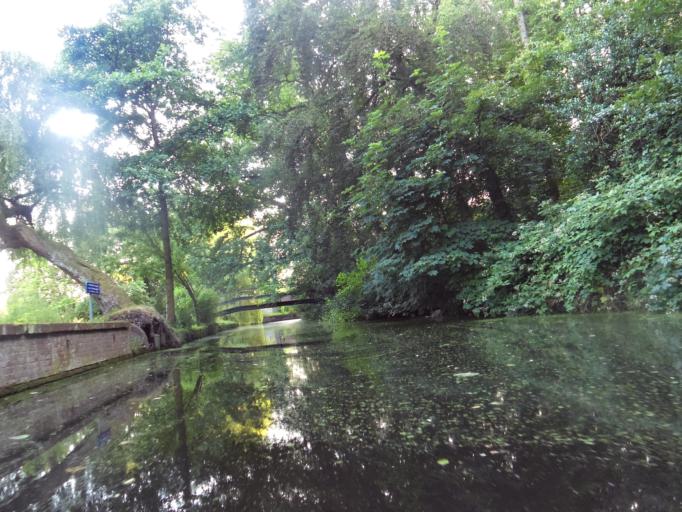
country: NL
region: South Holland
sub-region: Gemeente Wassenaar
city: Wassenaar
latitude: 52.1358
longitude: 4.3952
